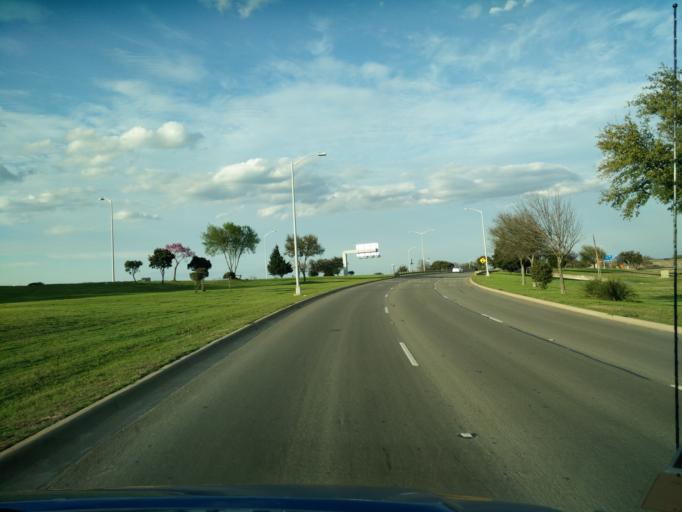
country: US
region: Texas
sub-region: Travis County
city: Hornsby Bend
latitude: 30.2095
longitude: -97.6625
